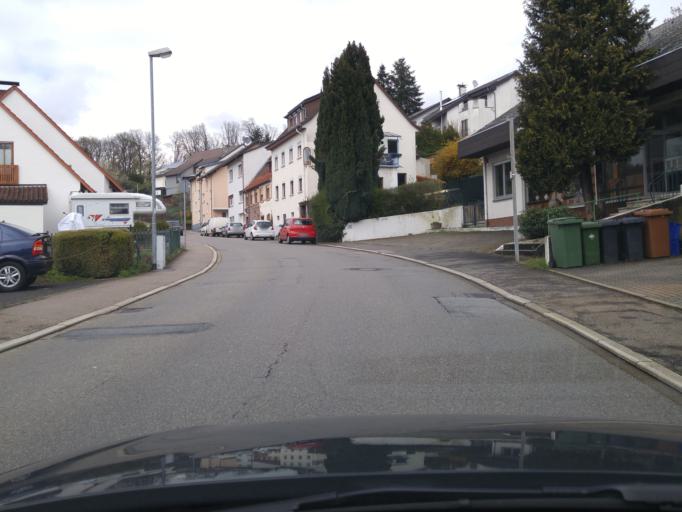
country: DE
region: Hesse
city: Neckarsteinach
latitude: 49.3937
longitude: 8.8419
